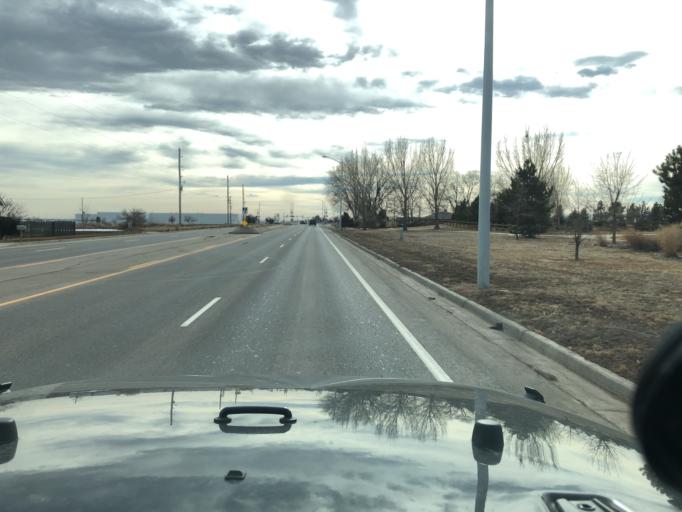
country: US
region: Colorado
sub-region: Boulder County
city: Longmont
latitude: 40.1695
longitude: -105.0554
